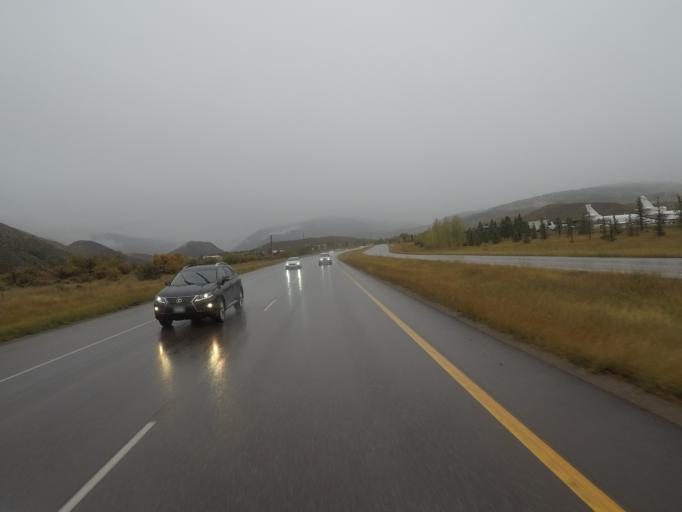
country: US
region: Colorado
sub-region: Pitkin County
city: Aspen
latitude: 39.2299
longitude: -106.8687
